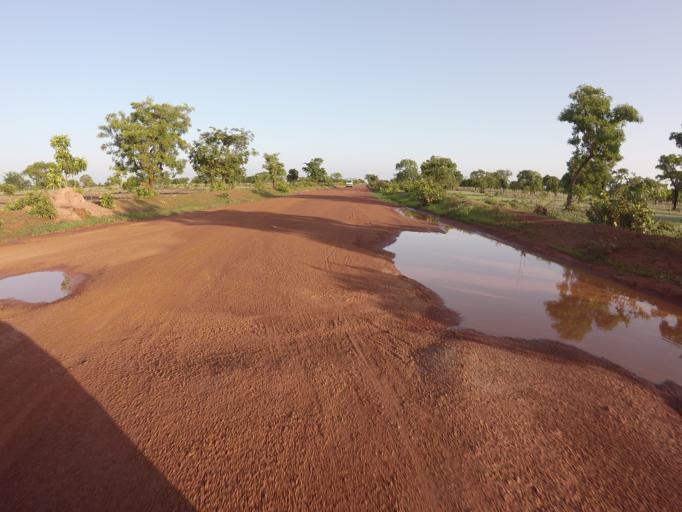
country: TG
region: Savanes
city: Sansanne-Mango
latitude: 10.2727
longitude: -0.0822
